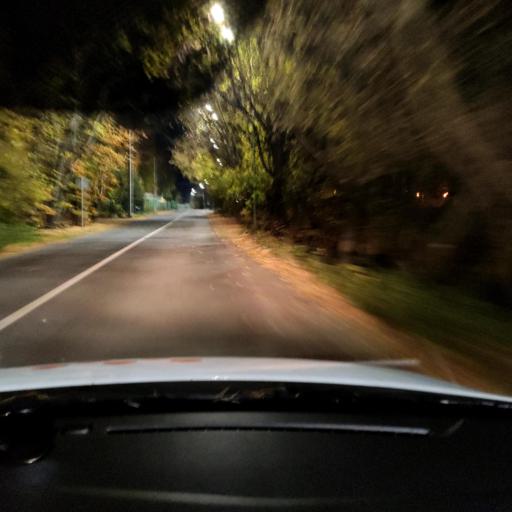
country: RU
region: Tatarstan
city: Verkhniy Uslon
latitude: 55.6239
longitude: 49.0137
